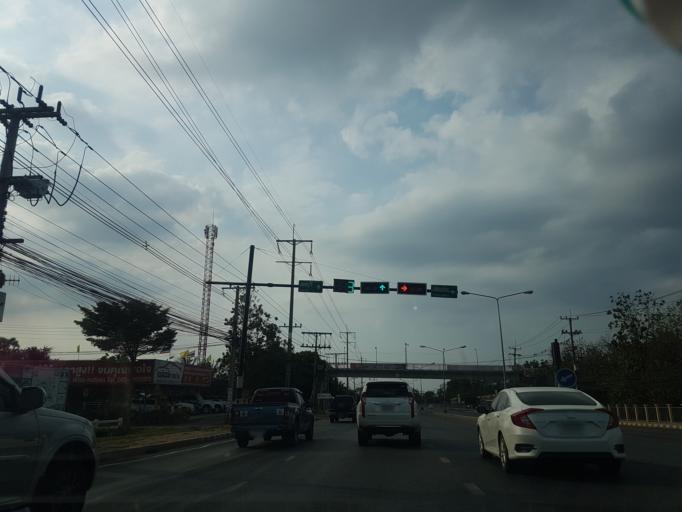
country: TH
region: Sara Buri
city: Phra Phutthabat
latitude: 14.7345
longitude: 100.7781
